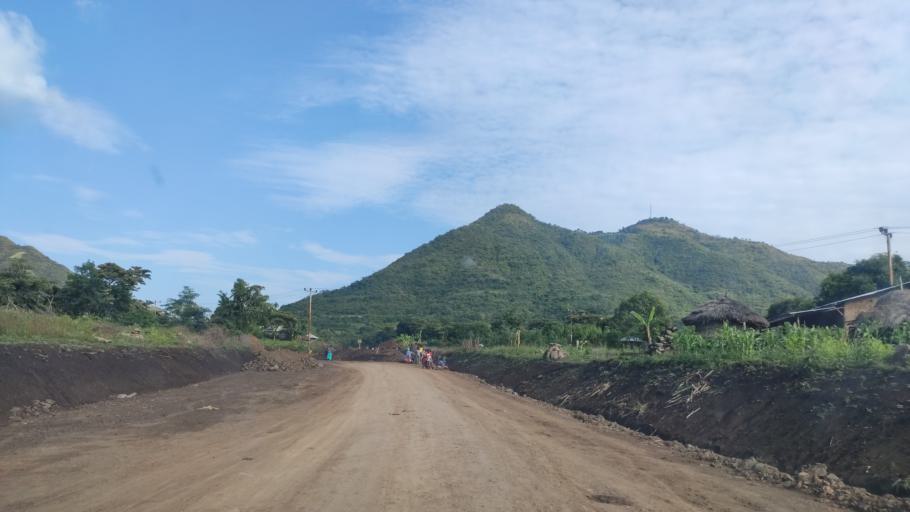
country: ET
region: Southern Nations, Nationalities, and People's Region
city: Arba Minch'
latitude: 6.4261
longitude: 37.3333
